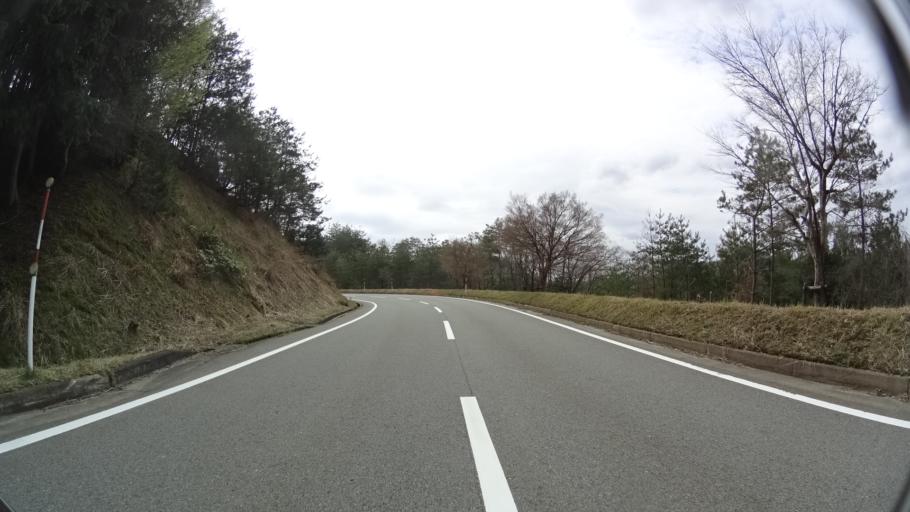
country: JP
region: Hyogo
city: Toyooka
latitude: 35.5062
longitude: 134.9017
